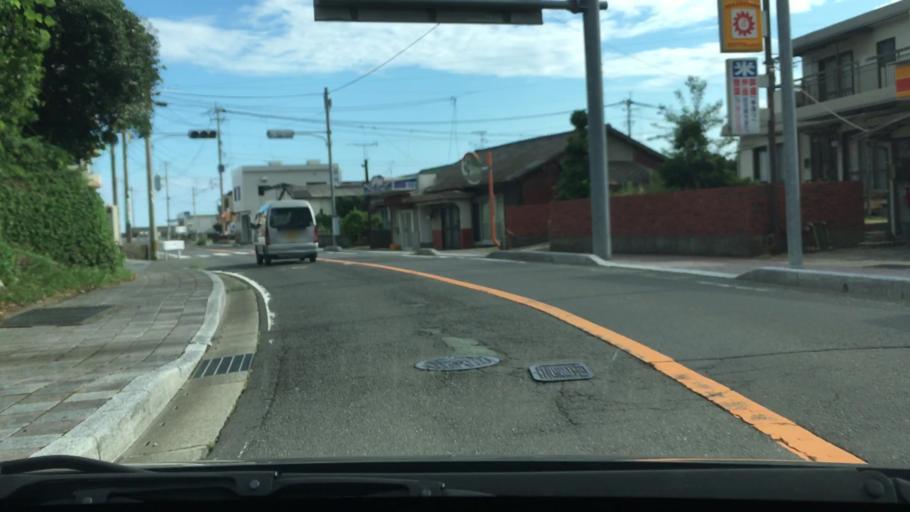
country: JP
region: Nagasaki
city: Togitsu
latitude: 32.8370
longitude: 129.7141
